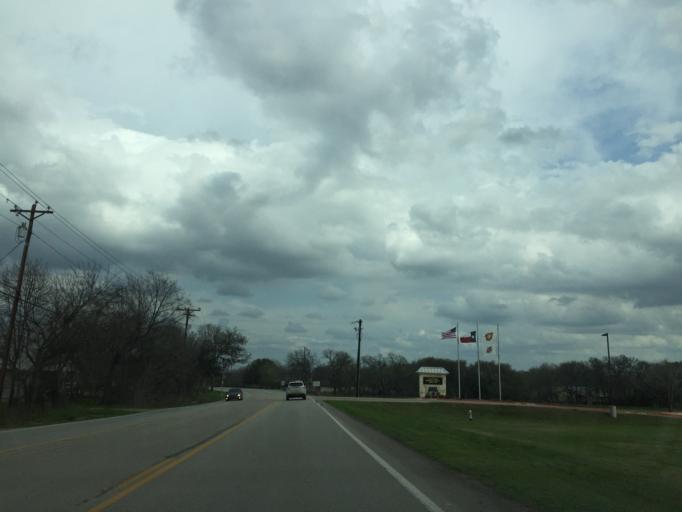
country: US
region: Texas
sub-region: Travis County
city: Manchaca
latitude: 30.1406
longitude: -97.8251
